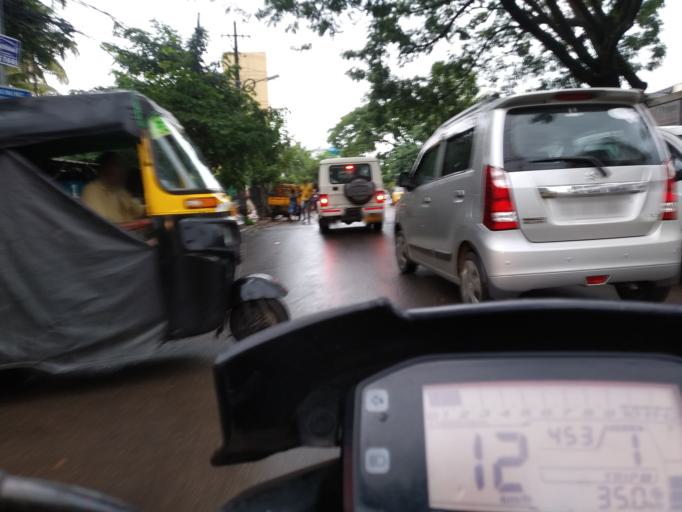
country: IN
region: Kerala
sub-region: Ernakulam
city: Cochin
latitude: 9.9723
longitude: 76.3045
